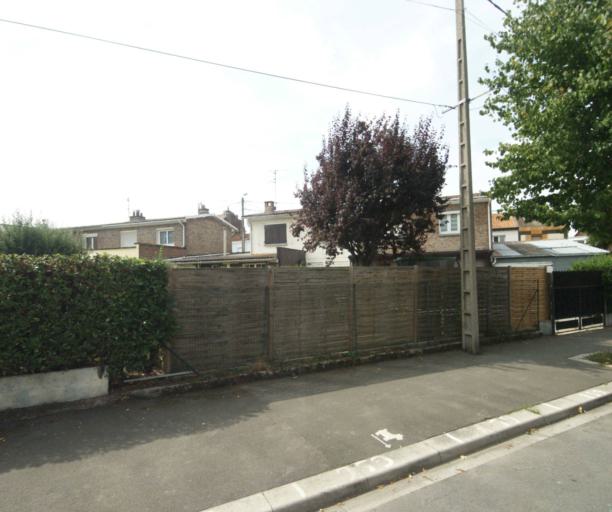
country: FR
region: Nord-Pas-de-Calais
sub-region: Departement du Nord
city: Loos
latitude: 50.6105
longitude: 3.0244
